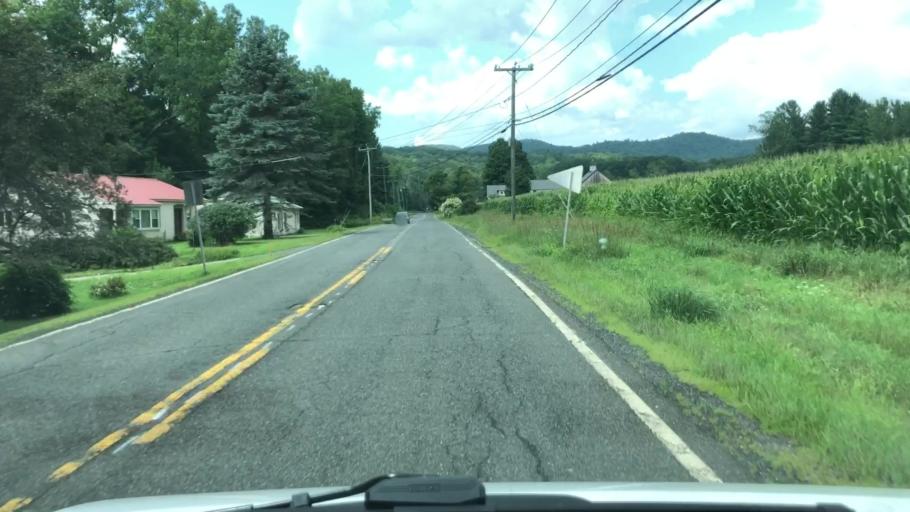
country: US
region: Massachusetts
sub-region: Franklin County
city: Conway
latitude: 42.5116
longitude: -72.7141
